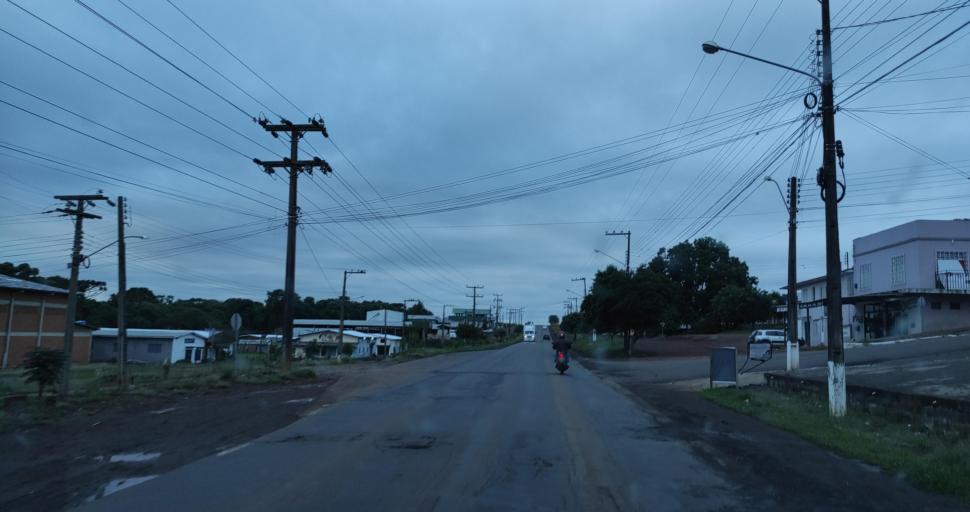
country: BR
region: Santa Catarina
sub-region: Xanxere
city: Xanxere
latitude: -26.7371
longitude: -52.3932
